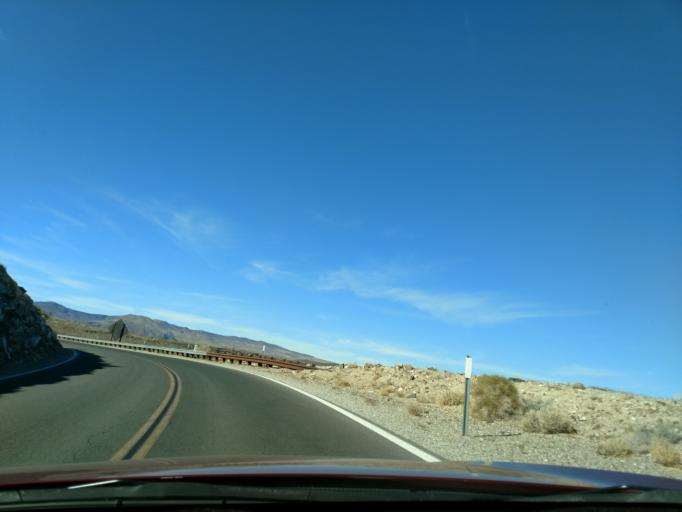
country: US
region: California
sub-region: Inyo County
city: Lone Pine
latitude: 36.3798
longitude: -117.5948
